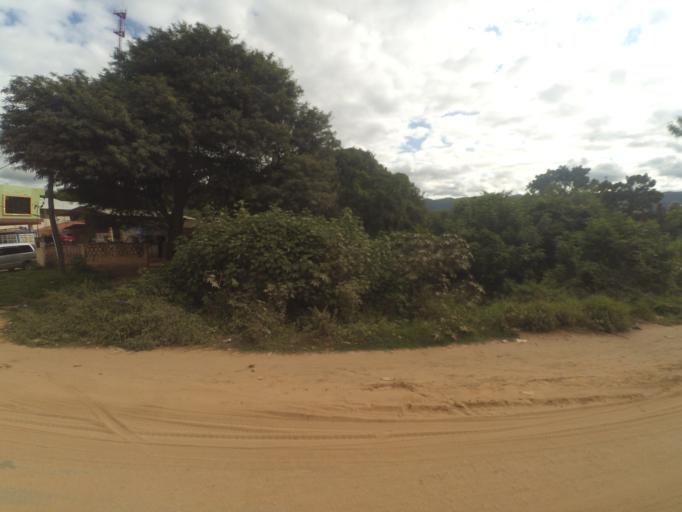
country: BO
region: Santa Cruz
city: Samaipata
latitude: -18.1637
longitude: -63.9226
